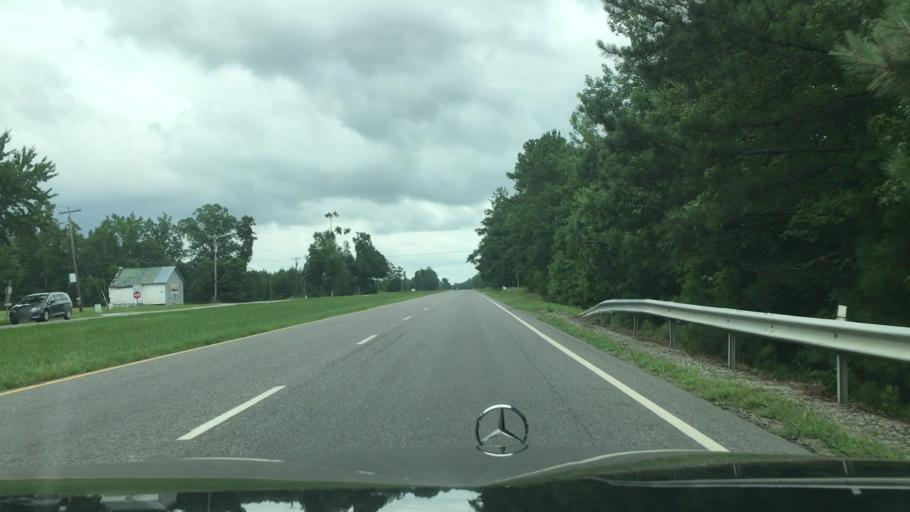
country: US
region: Virginia
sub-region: Chesterfield County
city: Woodlake
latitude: 37.3940
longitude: -77.7767
